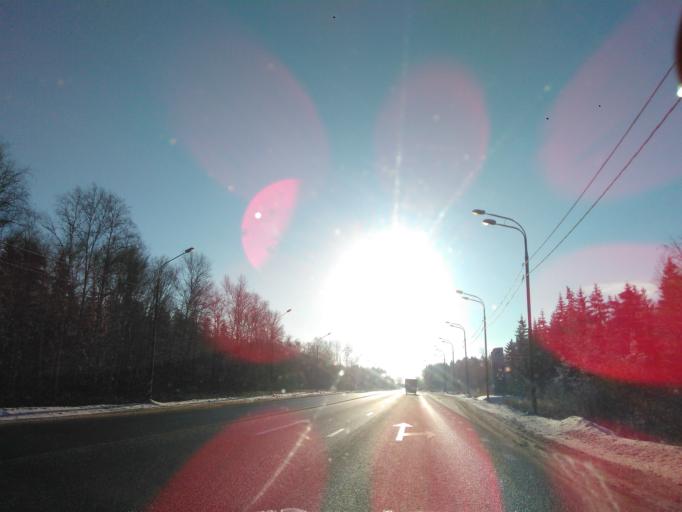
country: RU
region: Moskovskaya
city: Reshetnikovo
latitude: 56.4057
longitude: 36.6477
